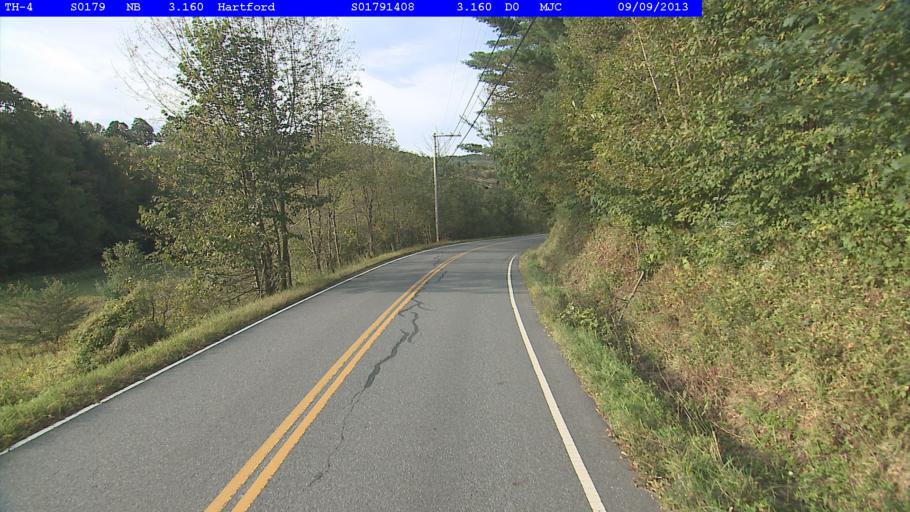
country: US
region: Vermont
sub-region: Windsor County
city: Woodstock
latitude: 43.6861
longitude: -72.4449
